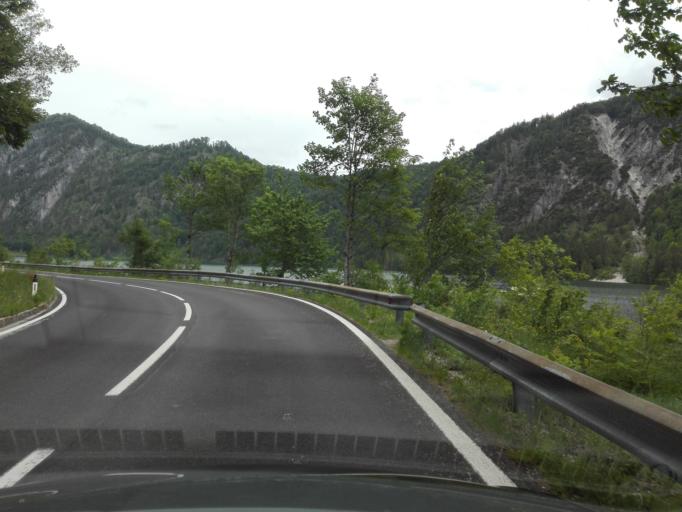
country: AT
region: Upper Austria
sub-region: Politischer Bezirk Gmunden
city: Gruenau im Almtal
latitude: 47.7486
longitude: 13.9527
